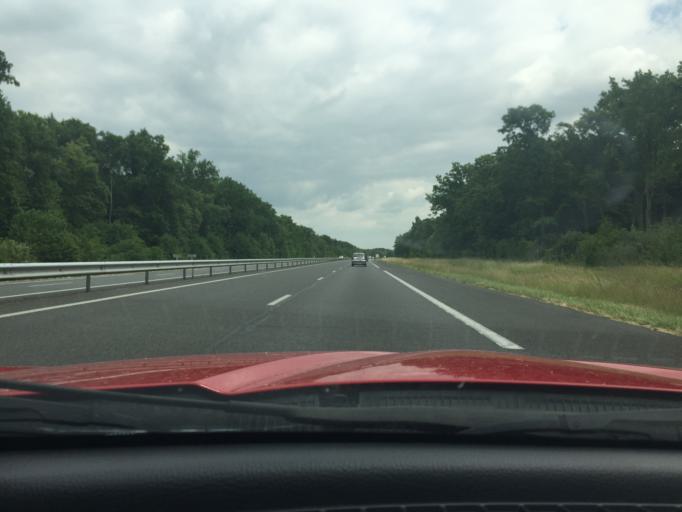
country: FR
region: Picardie
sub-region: Departement de l'Aisne
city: Liesse-Notre-Dame
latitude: 49.5637
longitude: 3.7660
